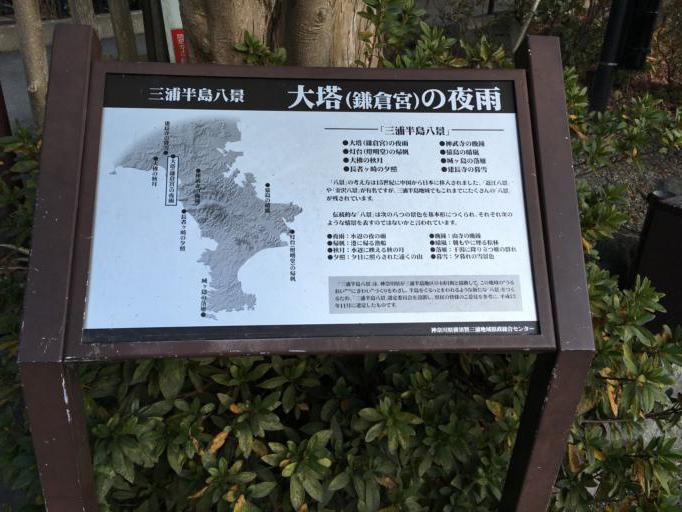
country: JP
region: Kanagawa
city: Kamakura
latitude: 35.3257
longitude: 139.5661
